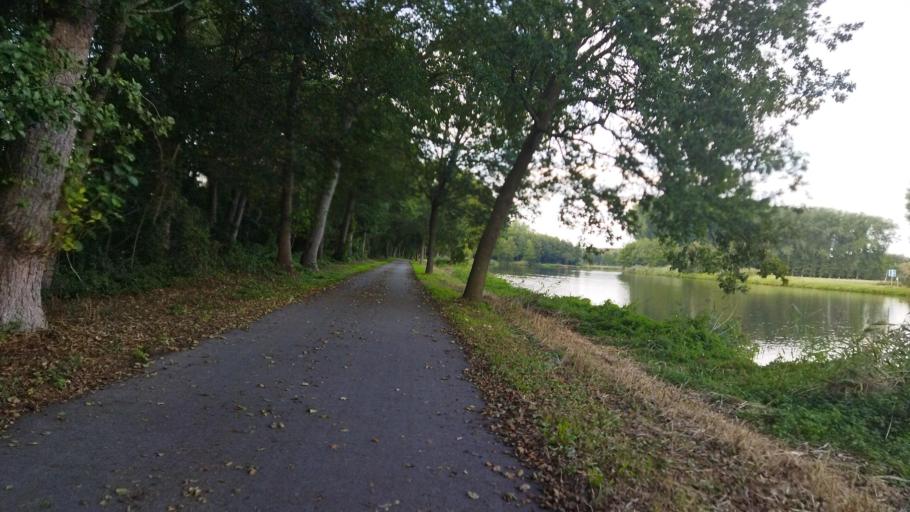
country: DE
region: Lower Saxony
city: Dersum
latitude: 52.9525
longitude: 7.2924
